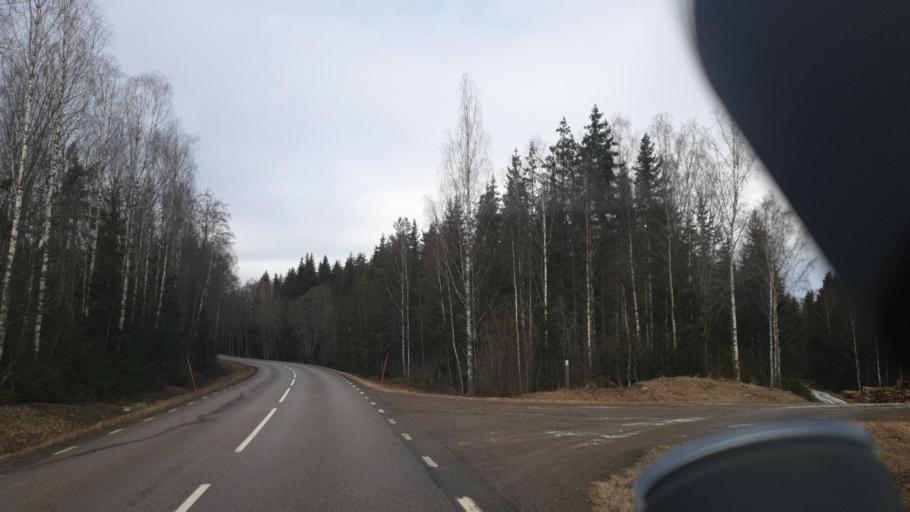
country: SE
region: Vaermland
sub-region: Arvika Kommun
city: Arvika
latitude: 59.5036
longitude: 12.6791
